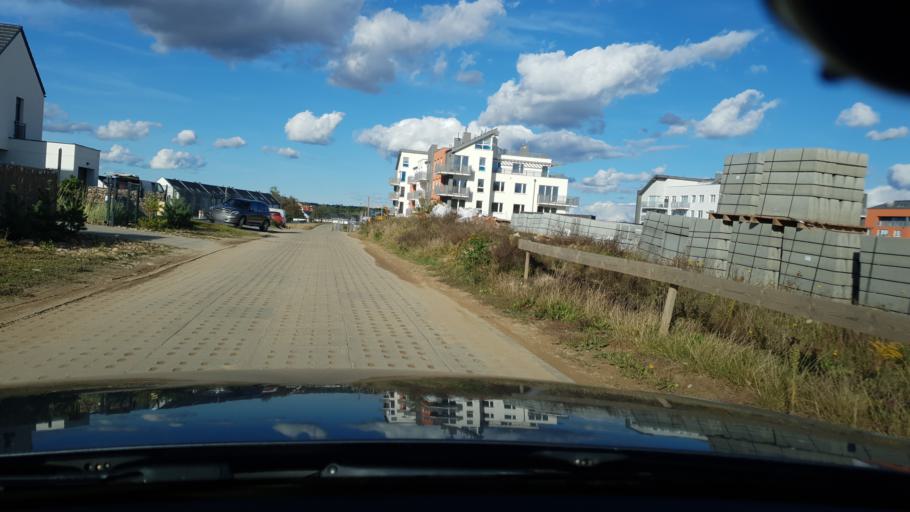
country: PL
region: Pomeranian Voivodeship
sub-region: Powiat wejherowski
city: Bojano
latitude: 54.4864
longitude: 18.4232
